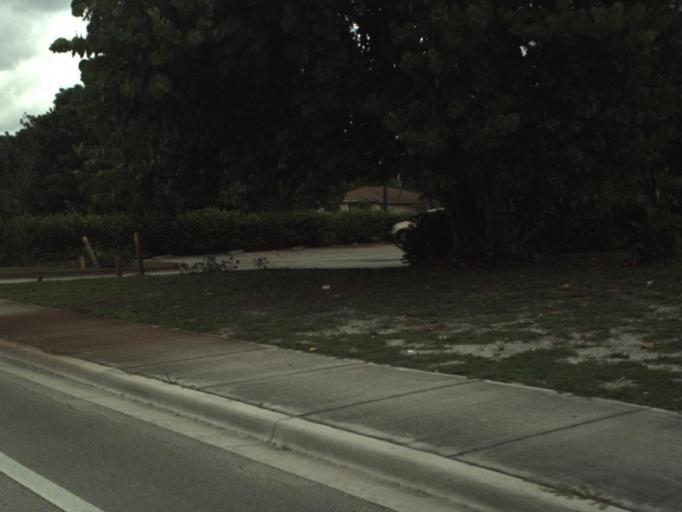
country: US
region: Florida
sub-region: Broward County
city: Deerfield Beach
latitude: 26.3142
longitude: -80.1028
